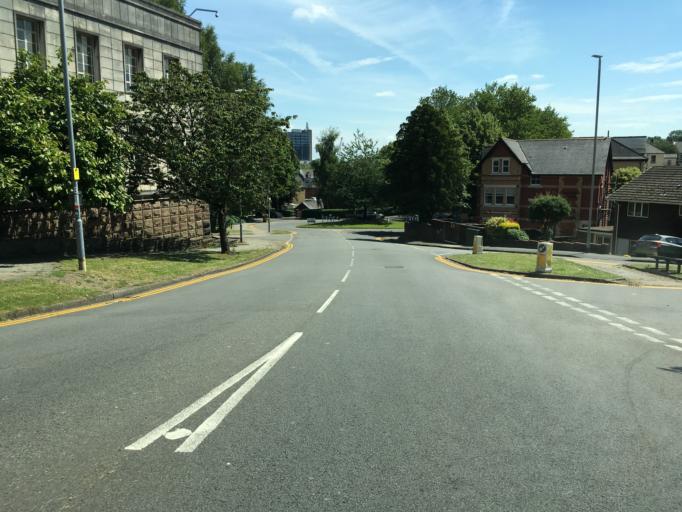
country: GB
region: Wales
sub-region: Newport
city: Newport
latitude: 51.5879
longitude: -3.0060
